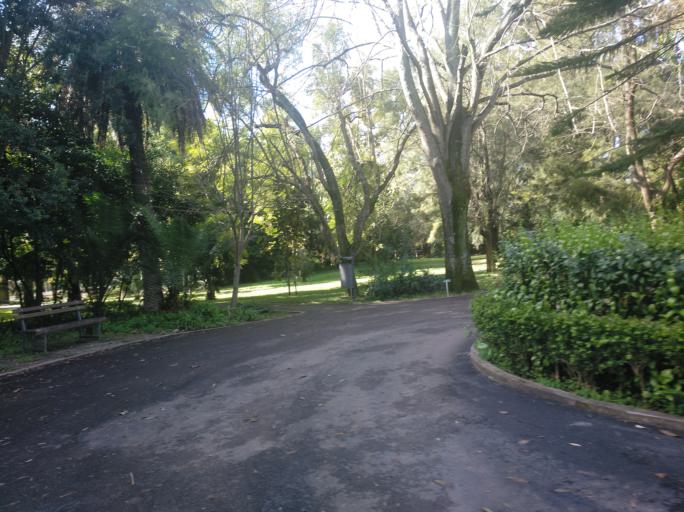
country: PT
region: Lisbon
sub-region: Oeiras
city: Alges
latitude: 38.6995
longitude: -9.2021
